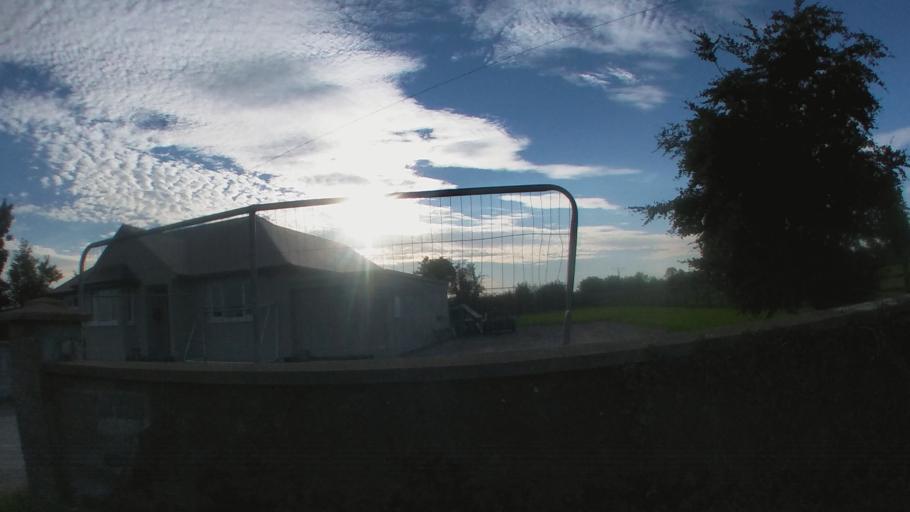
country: IE
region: Leinster
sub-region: Kilkenny
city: Kilkenny
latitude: 52.6719
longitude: -7.2289
